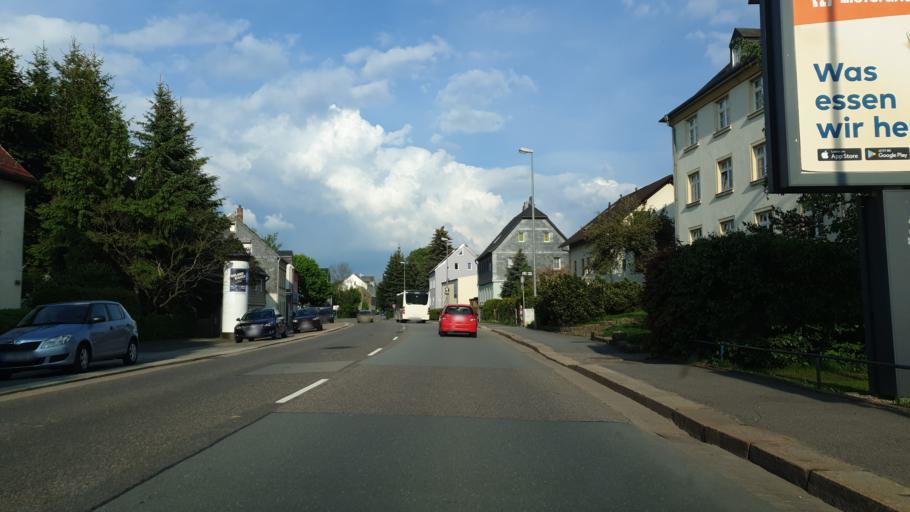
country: DE
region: Saxony
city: Neukirchen
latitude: 50.8194
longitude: 12.8609
